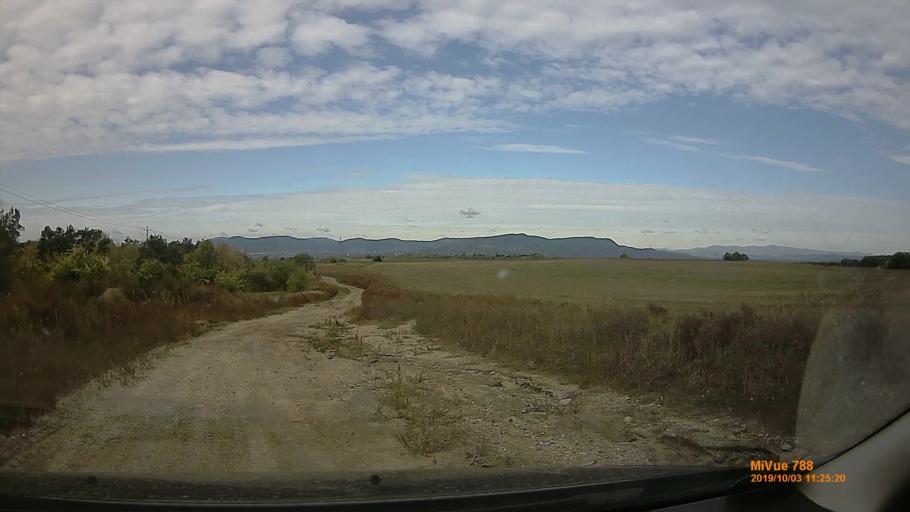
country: HU
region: Pest
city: Fot
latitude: 47.6517
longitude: 19.1738
